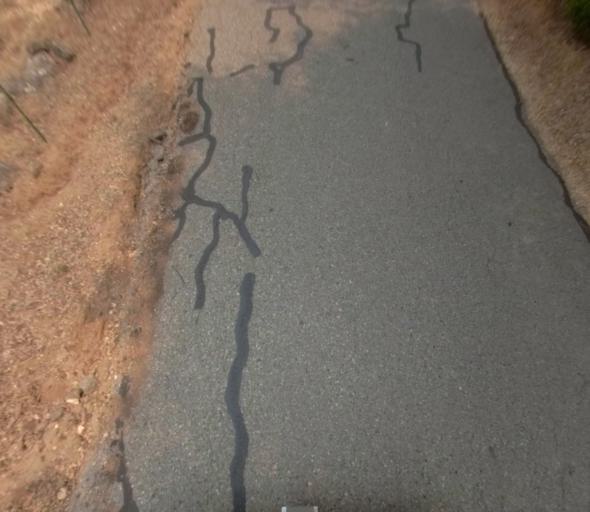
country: US
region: California
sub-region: Madera County
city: Oakhurst
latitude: 37.2934
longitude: -119.6519
